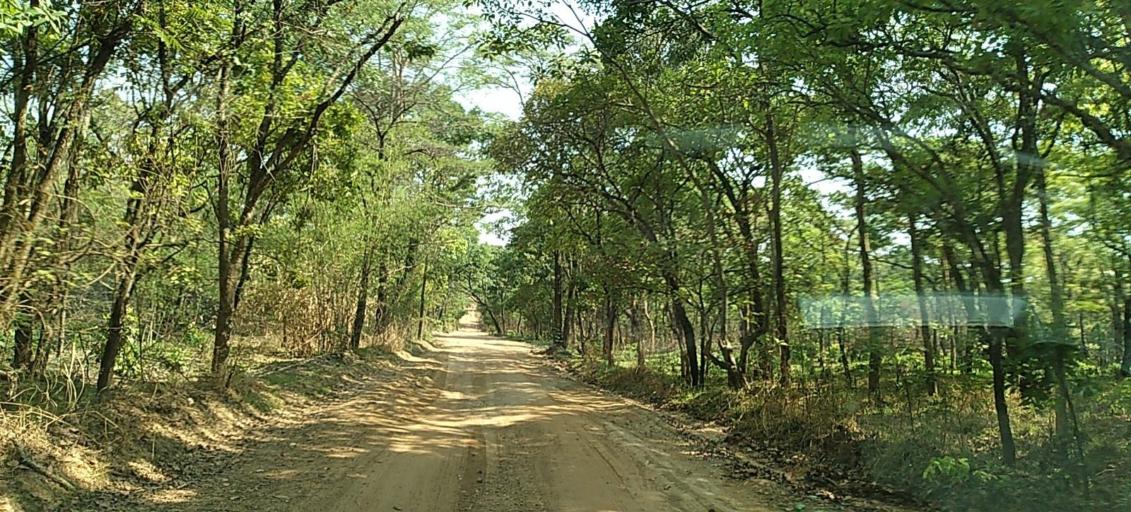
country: ZM
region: Copperbelt
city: Kalulushi
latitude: -12.9371
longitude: 27.8212
